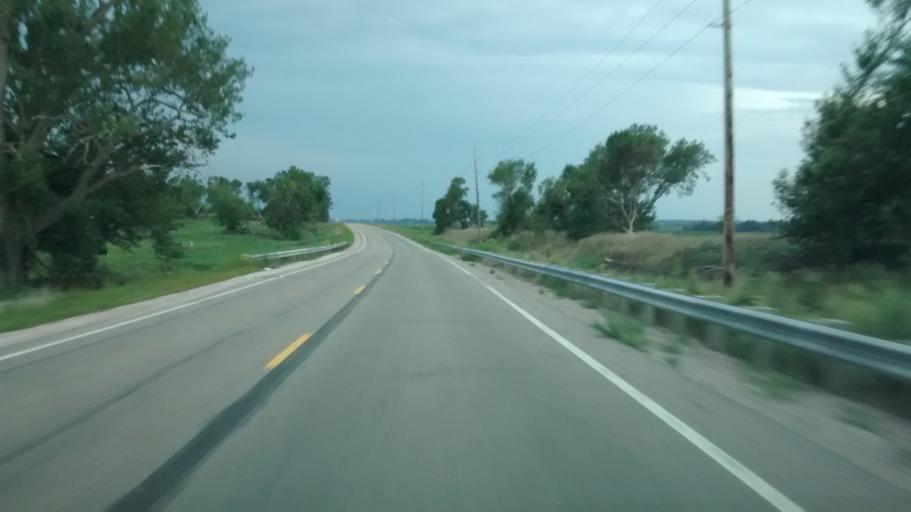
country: US
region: Iowa
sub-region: Plymouth County
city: Kingsley
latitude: 42.5616
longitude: -96.0101
